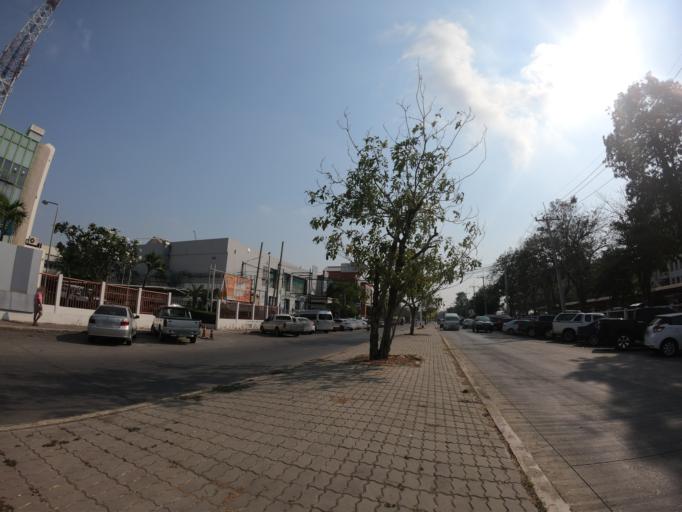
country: TH
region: Phra Nakhon Si Ayutthaya
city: Phra Nakhon Si Ayutthaya
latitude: 14.3348
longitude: 100.6098
